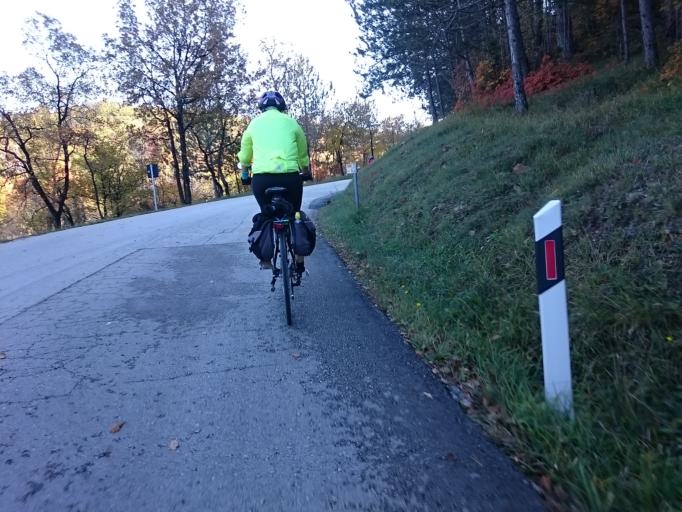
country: HR
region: Istarska
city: Buje
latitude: 45.3895
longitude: 13.7221
